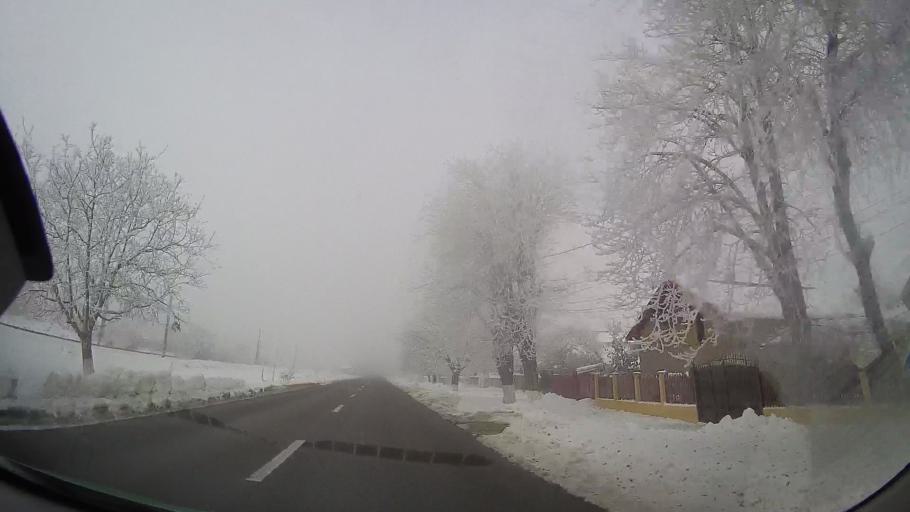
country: RO
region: Iasi
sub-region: Comuna Mircesti
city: Mircesti
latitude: 47.0880
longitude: 26.8249
